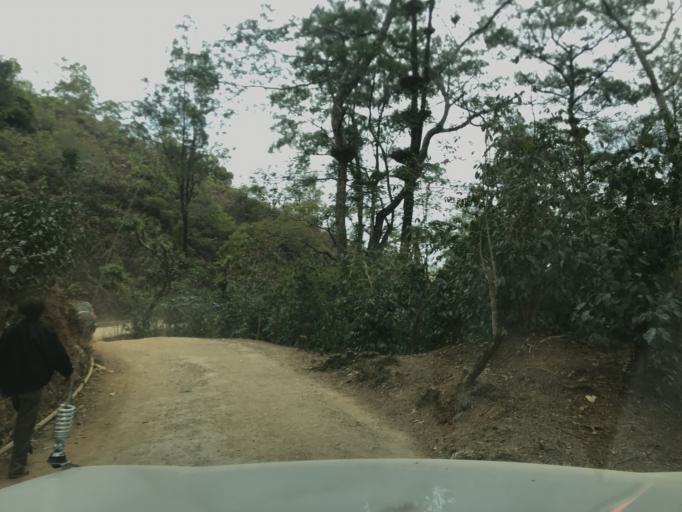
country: TL
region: Ermera
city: Gleno
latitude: -8.8363
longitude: 125.4448
